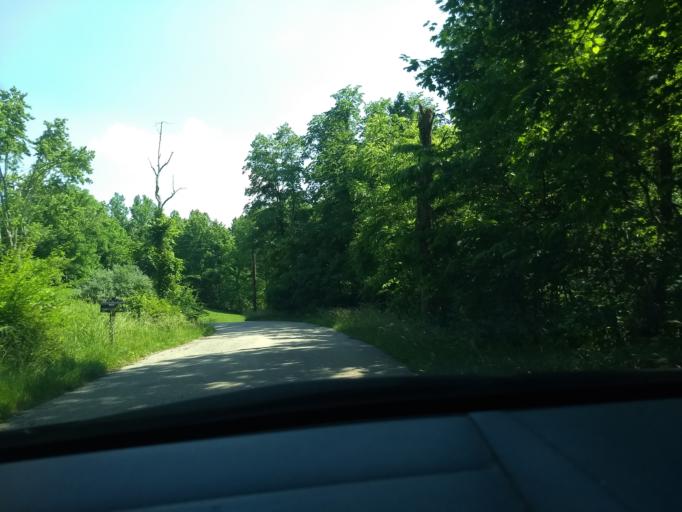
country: US
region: Indiana
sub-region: Floyd County
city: New Albany
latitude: 38.2750
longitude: -85.8671
